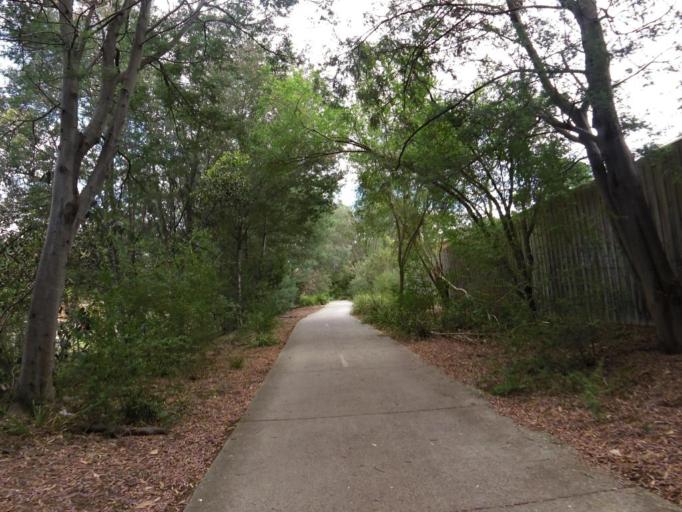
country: AU
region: Victoria
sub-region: Monash
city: Ashwood
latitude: -37.8658
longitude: 145.1007
